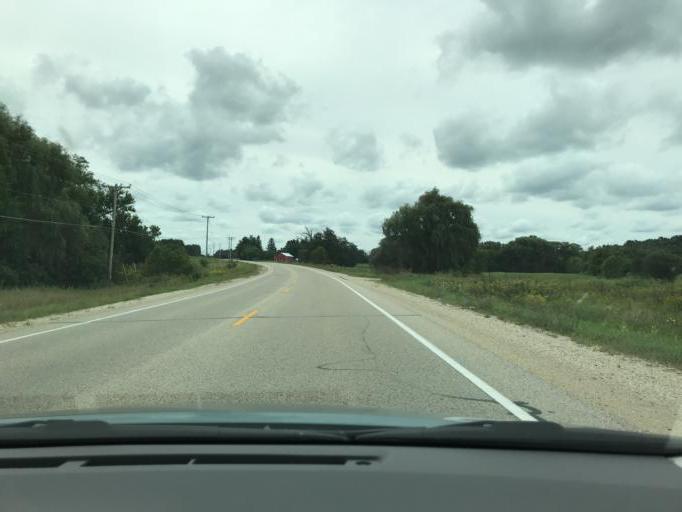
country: US
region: Wisconsin
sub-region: Racine County
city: Bohners Lake
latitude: 42.6307
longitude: -88.2471
